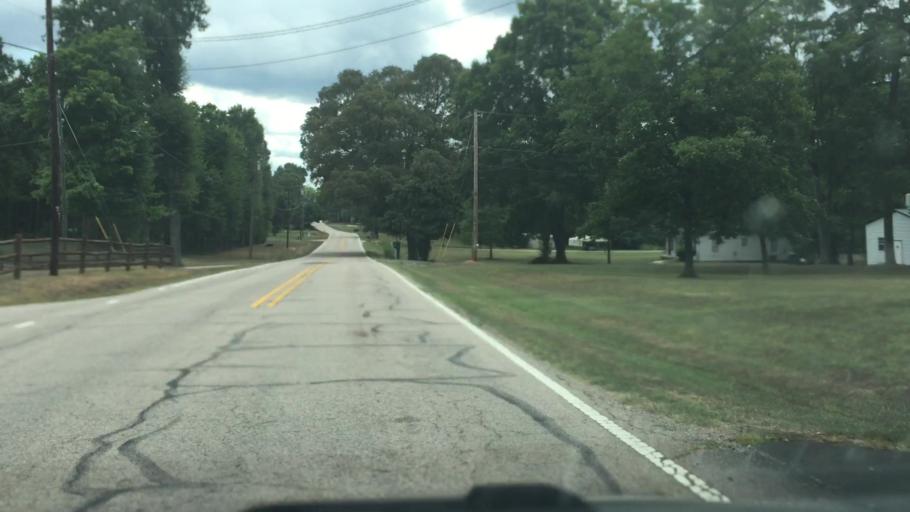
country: US
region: North Carolina
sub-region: Rowan County
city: Enochville
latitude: 35.5045
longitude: -80.6712
